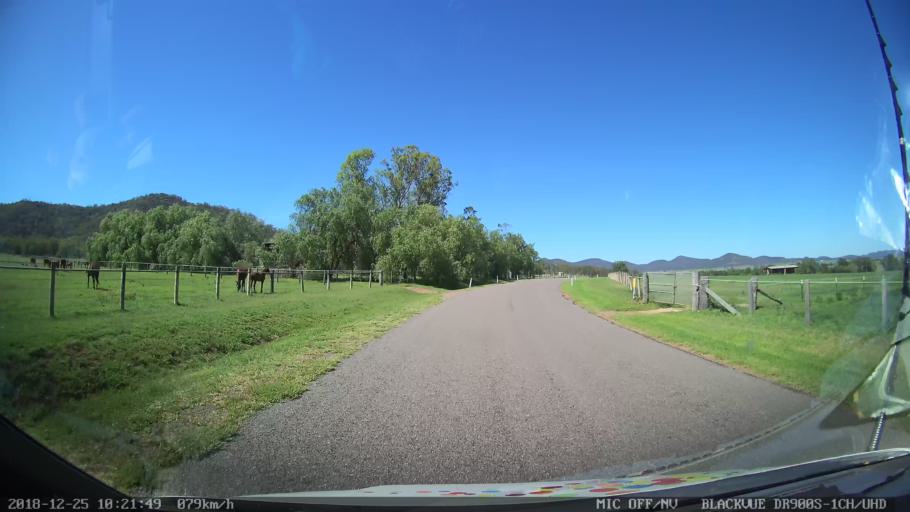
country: AU
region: New South Wales
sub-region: Muswellbrook
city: Denman
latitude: -32.3716
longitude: 150.5391
